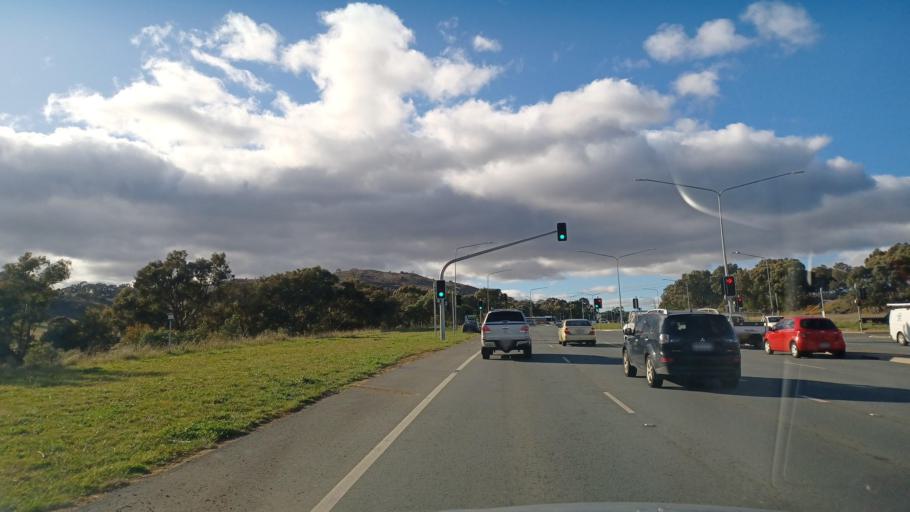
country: AU
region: Australian Capital Territory
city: Macquarie
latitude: -35.2690
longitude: 149.0507
